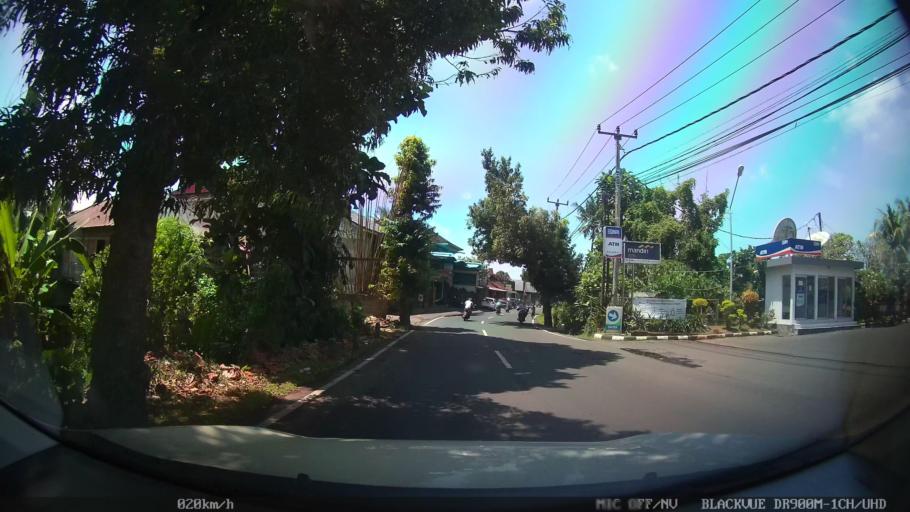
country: ID
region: Bali
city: Banjar Sedang
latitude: -8.5661
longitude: 115.3049
